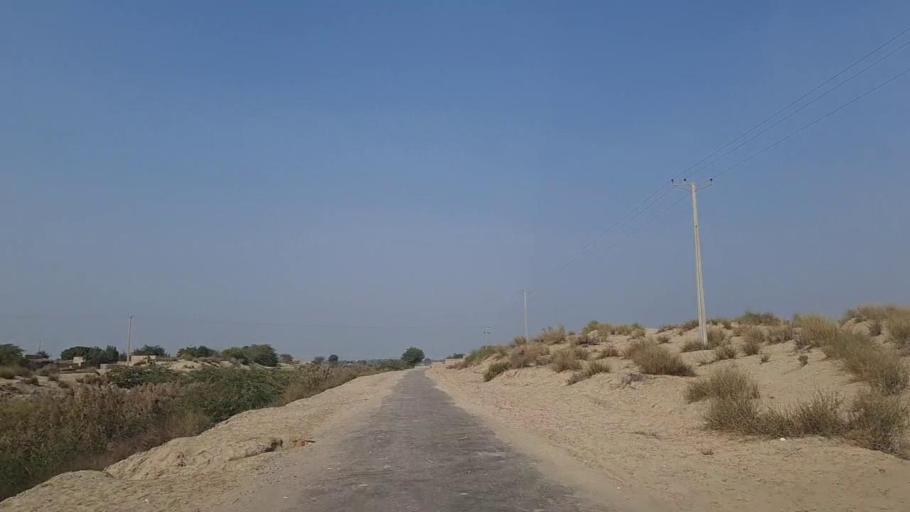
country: PK
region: Sindh
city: Daur
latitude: 26.4628
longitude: 68.4679
